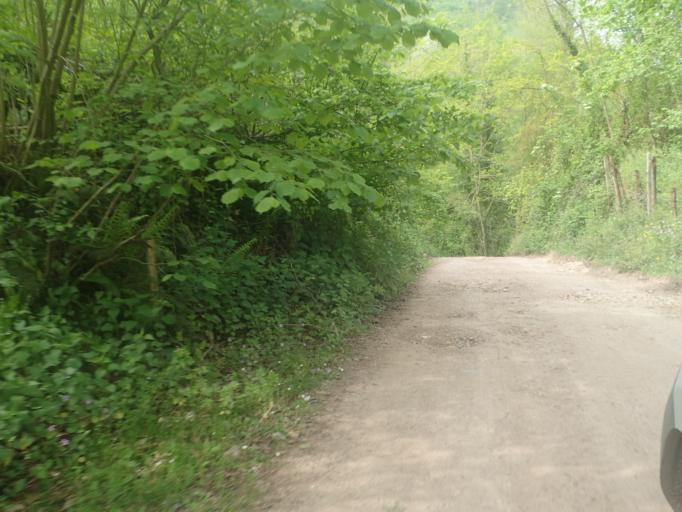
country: TR
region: Ordu
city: Catalpinar
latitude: 40.8998
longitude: 37.4828
